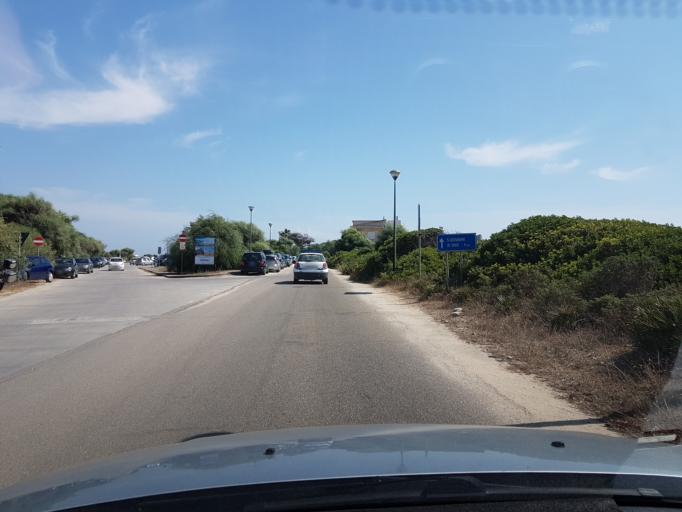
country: IT
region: Sardinia
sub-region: Provincia di Oristano
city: Cabras
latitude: 39.8845
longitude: 8.4378
